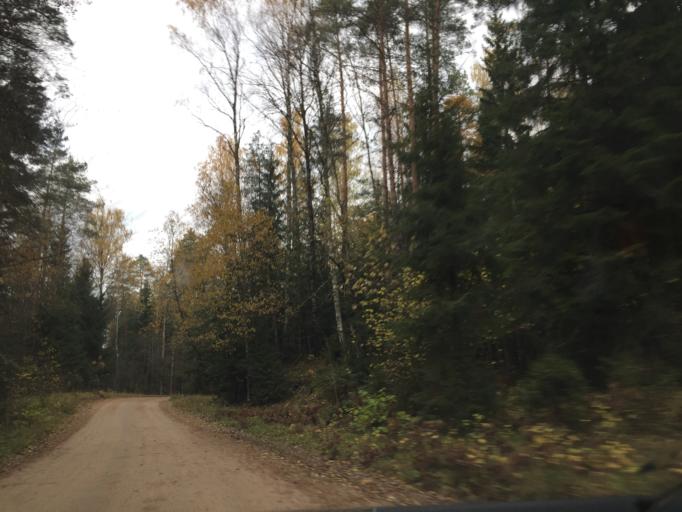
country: LV
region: Cesu Rajons
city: Cesis
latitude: 57.3418
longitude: 25.1576
